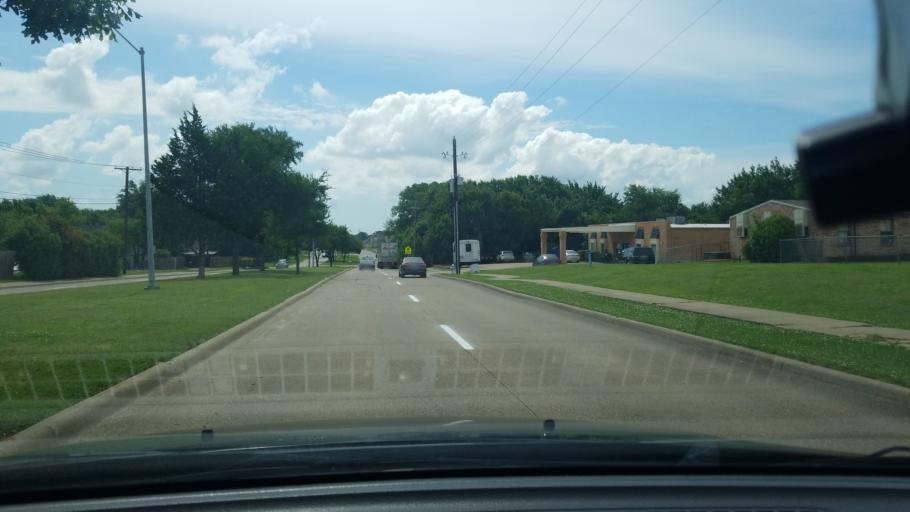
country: US
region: Texas
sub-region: Dallas County
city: Mesquite
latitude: 32.7636
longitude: -96.5804
